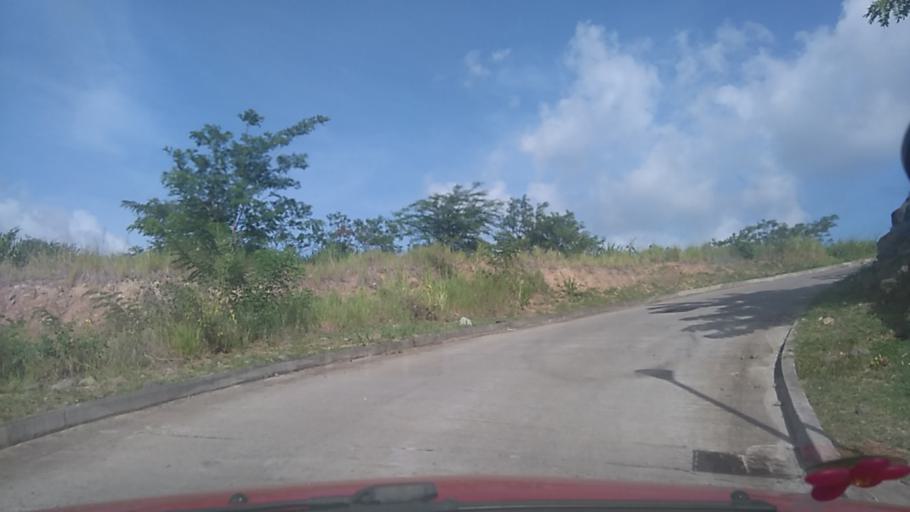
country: MQ
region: Martinique
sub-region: Martinique
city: Sainte-Luce
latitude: 14.4866
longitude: -60.9901
